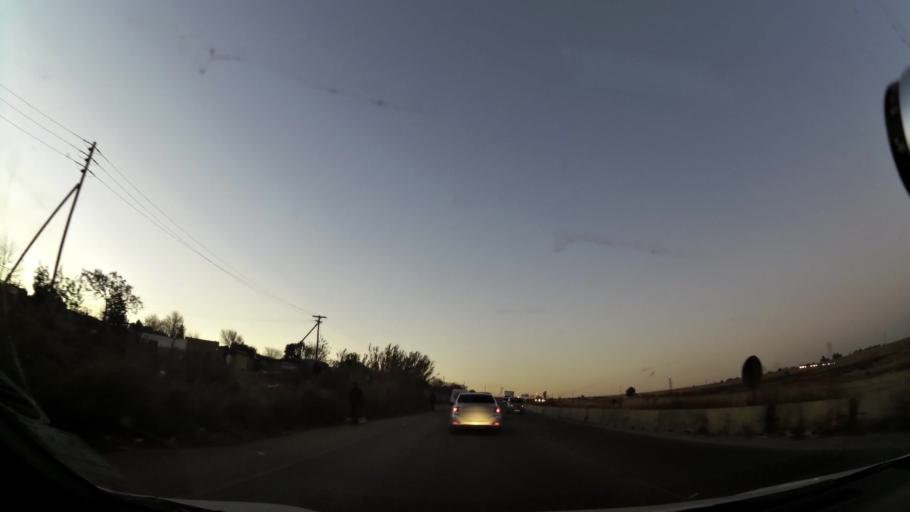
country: ZA
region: Gauteng
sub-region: City of Johannesburg Metropolitan Municipality
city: Diepsloot
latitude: -25.9210
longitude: 28.0231
